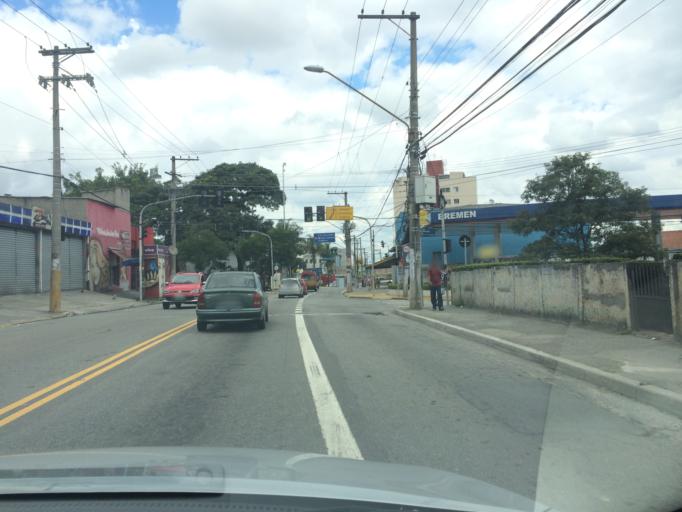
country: BR
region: Sao Paulo
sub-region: Guarulhos
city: Guarulhos
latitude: -23.4481
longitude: -46.5210
